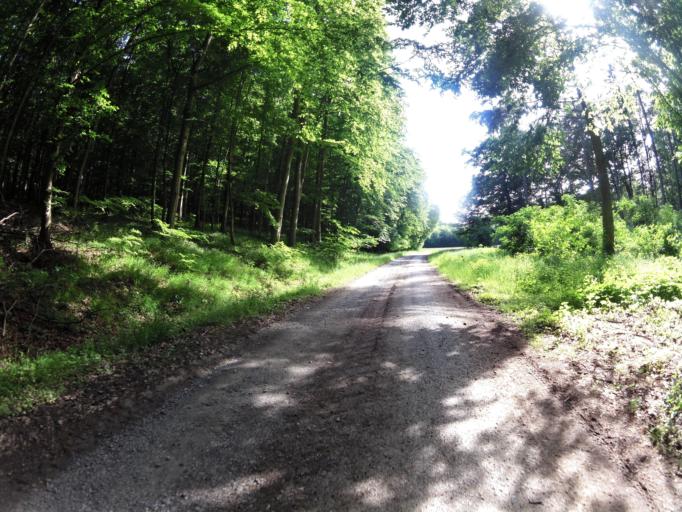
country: DE
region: Bavaria
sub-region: Regierungsbezirk Unterfranken
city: Uettingen
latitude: 49.7825
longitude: 9.7437
